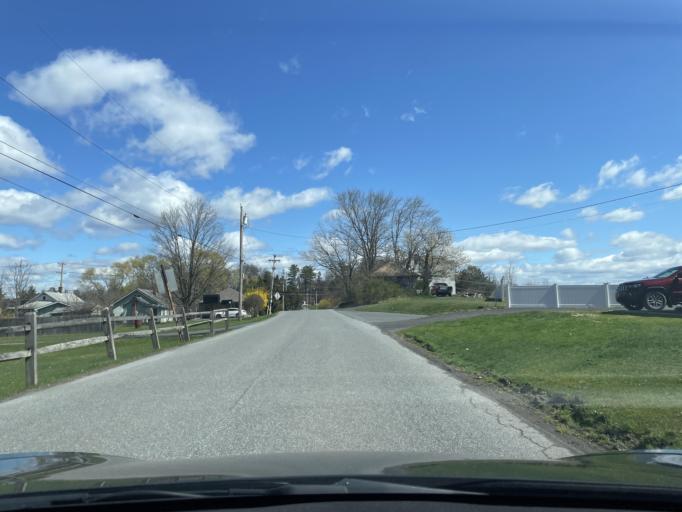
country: US
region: New York
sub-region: Ulster County
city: Saugerties
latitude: 42.0816
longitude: -73.9676
